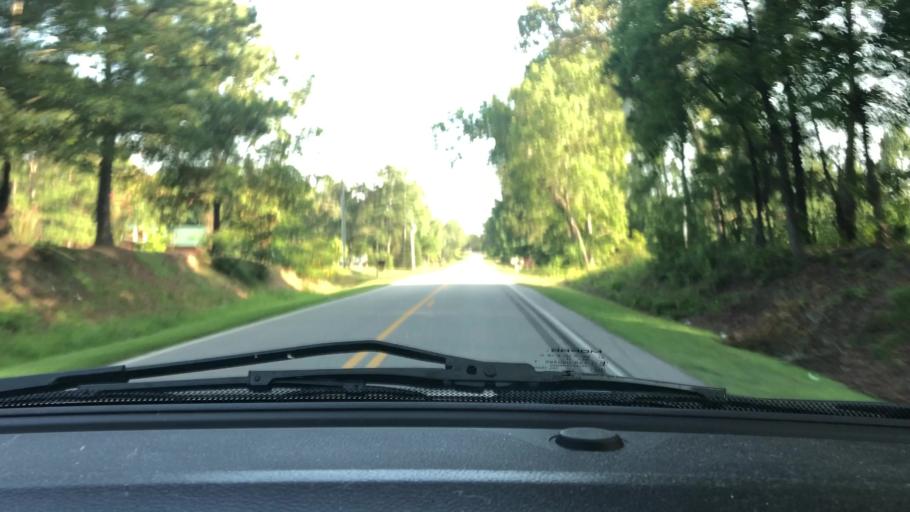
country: US
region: North Carolina
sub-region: Lee County
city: Broadway
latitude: 35.3301
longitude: -79.0719
